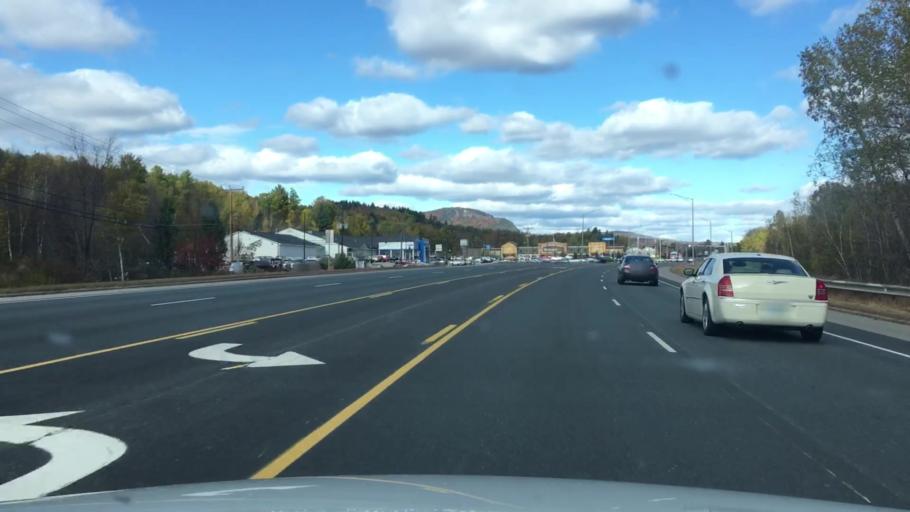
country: US
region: New Hampshire
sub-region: Coos County
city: Gorham
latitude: 44.4211
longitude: -71.1944
